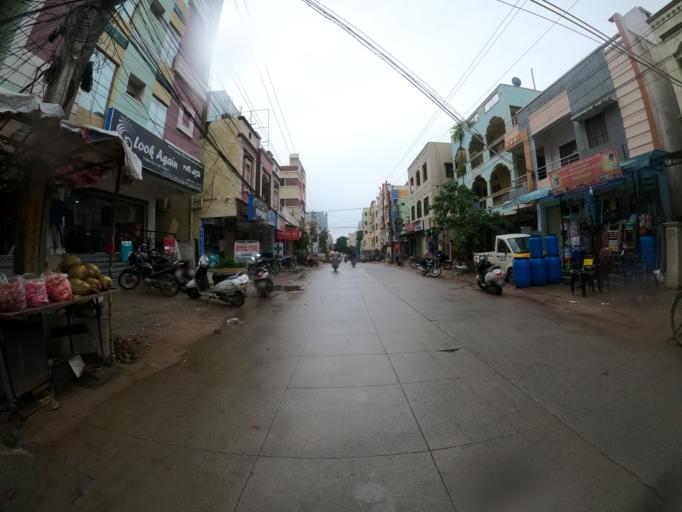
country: IN
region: Telangana
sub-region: Rangareddi
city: Kukatpalli
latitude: 17.4585
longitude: 78.4027
